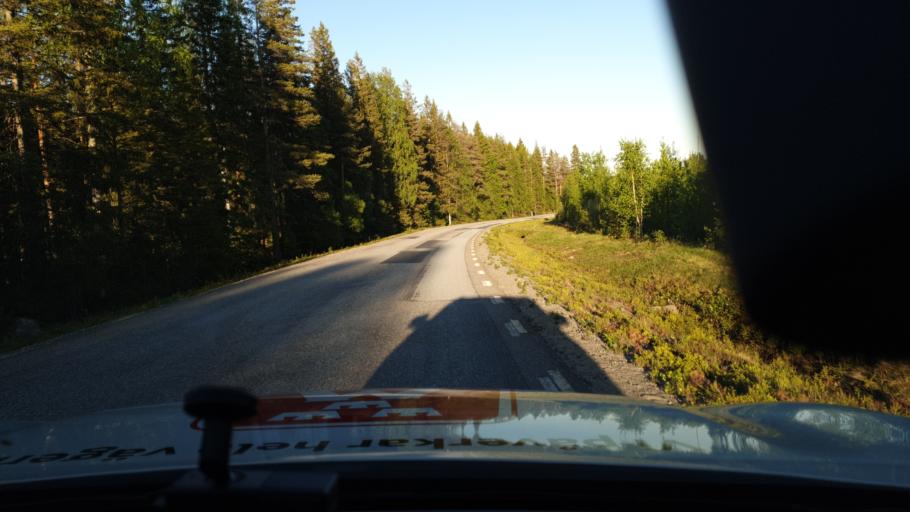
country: SE
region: Vaesterbotten
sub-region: Umea Kommun
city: Ersmark
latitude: 64.0101
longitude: 20.1883
